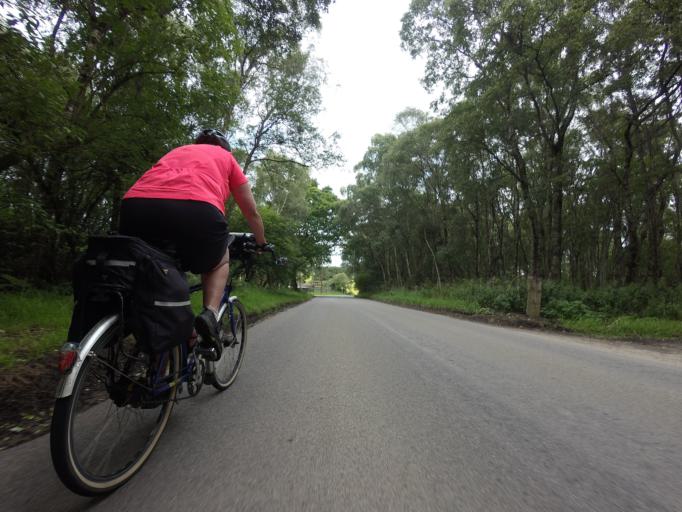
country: GB
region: Scotland
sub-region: Moray
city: Elgin
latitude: 57.6554
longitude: -3.3482
